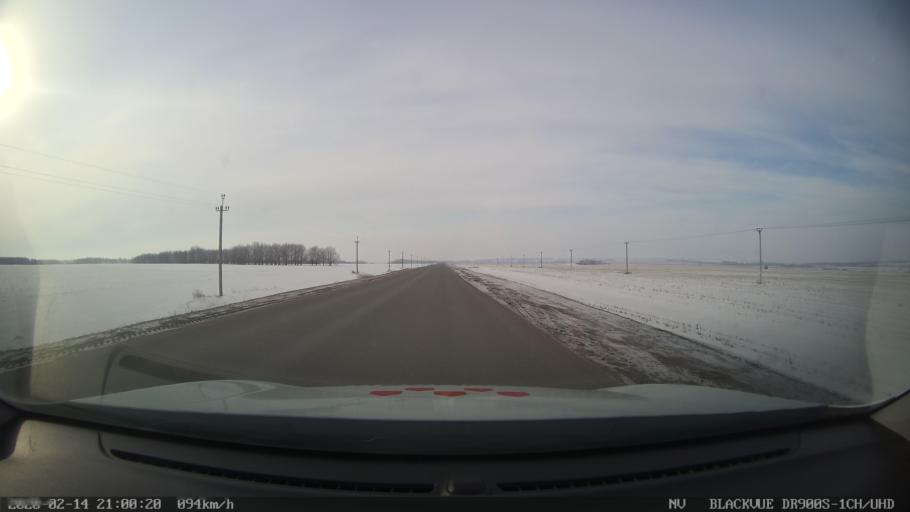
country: RU
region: Tatarstan
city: Kuybyshevskiy Zaton
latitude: 55.1718
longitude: 49.2218
